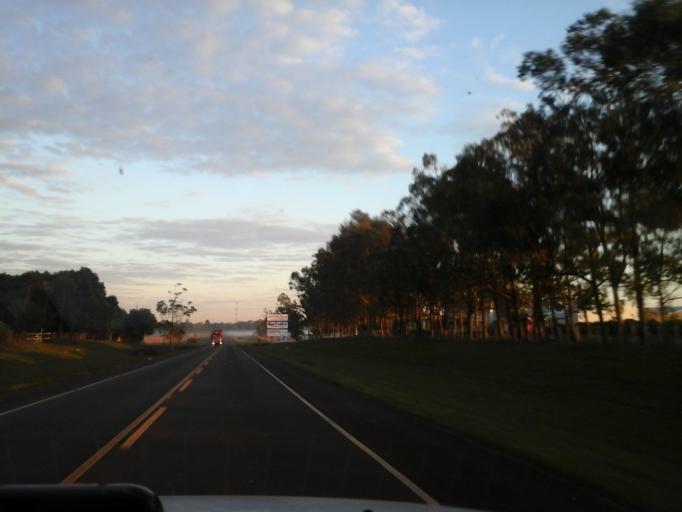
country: PY
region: Itapua
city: General Delgado
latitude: -27.0538
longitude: -56.6375
